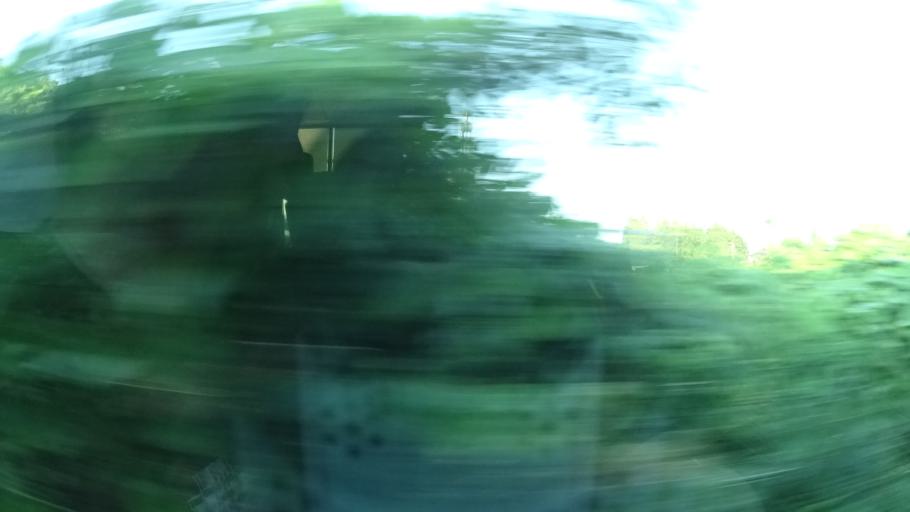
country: JP
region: Ibaraki
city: Ishioka
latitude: 36.2582
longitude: 140.2842
